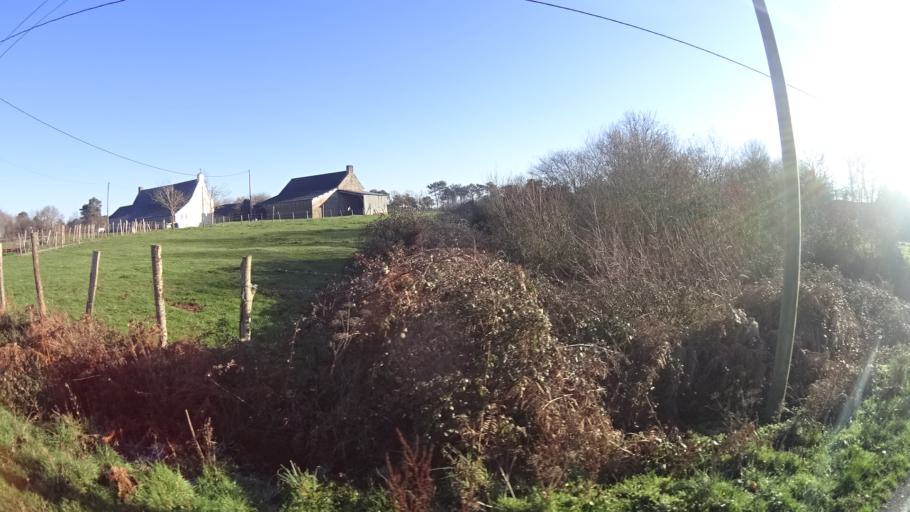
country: FR
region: Brittany
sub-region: Departement du Morbihan
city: Saint-Jacut-les-Pins
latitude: 47.6635
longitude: -2.1923
